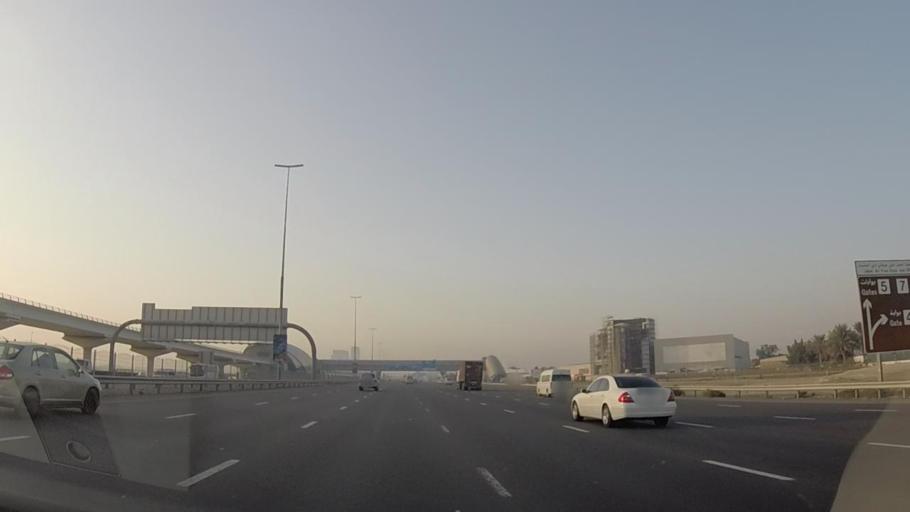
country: AE
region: Dubai
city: Dubai
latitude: 25.0040
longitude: 55.0955
